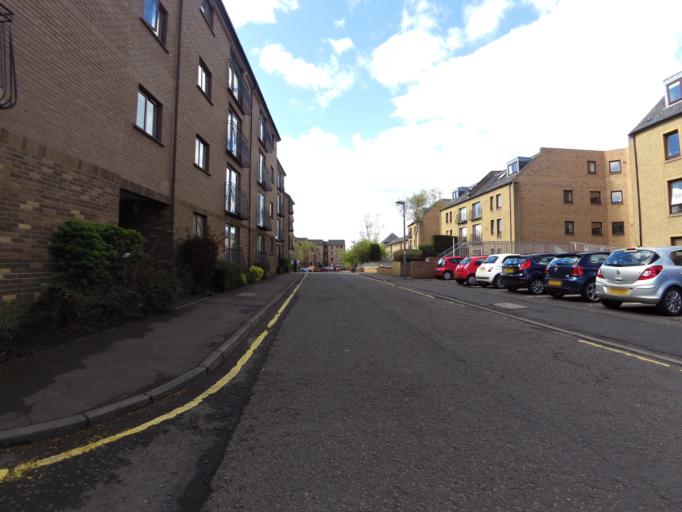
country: GB
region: Scotland
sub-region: Edinburgh
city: Edinburgh
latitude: 55.9414
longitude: -3.1725
